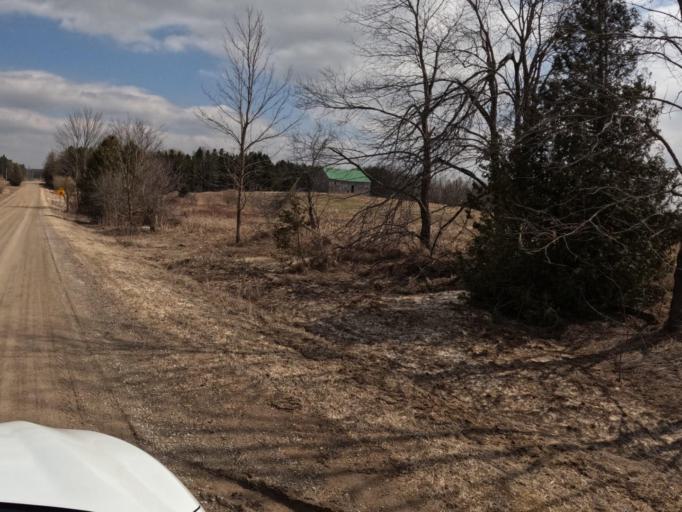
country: CA
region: Ontario
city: Shelburne
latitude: 44.0398
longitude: -80.1986
